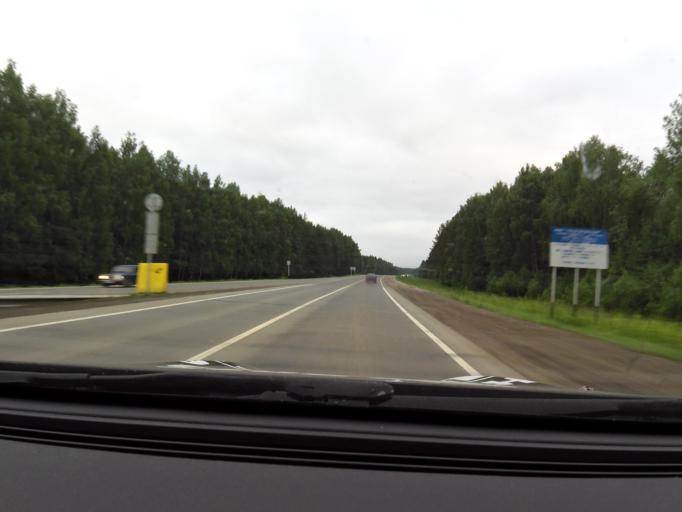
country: RU
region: Perm
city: Karagay
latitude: 58.2406
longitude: 54.9508
